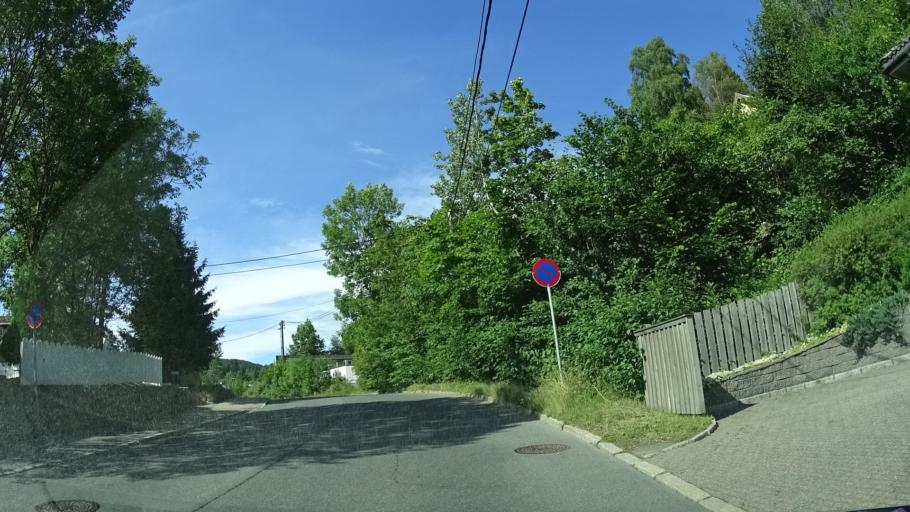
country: NO
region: Oslo
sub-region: Oslo
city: Sjolyststranda
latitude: 59.9549
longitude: 10.6910
